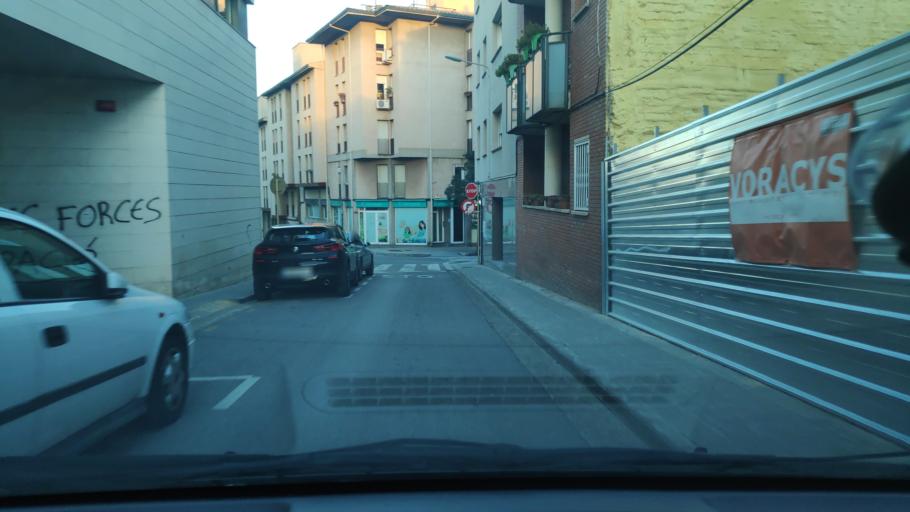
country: ES
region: Catalonia
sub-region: Provincia de Barcelona
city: Sant Quirze del Valles
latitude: 41.5322
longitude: 2.0825
